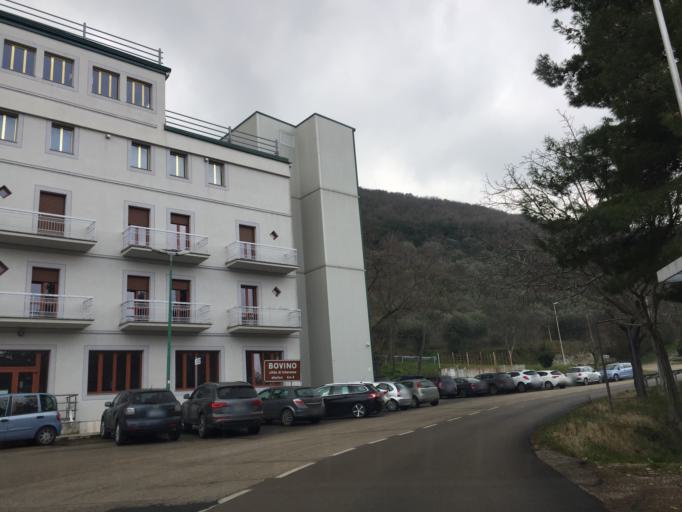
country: IT
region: Apulia
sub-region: Provincia di Foggia
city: Bovino
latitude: 41.2622
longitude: 15.3601
